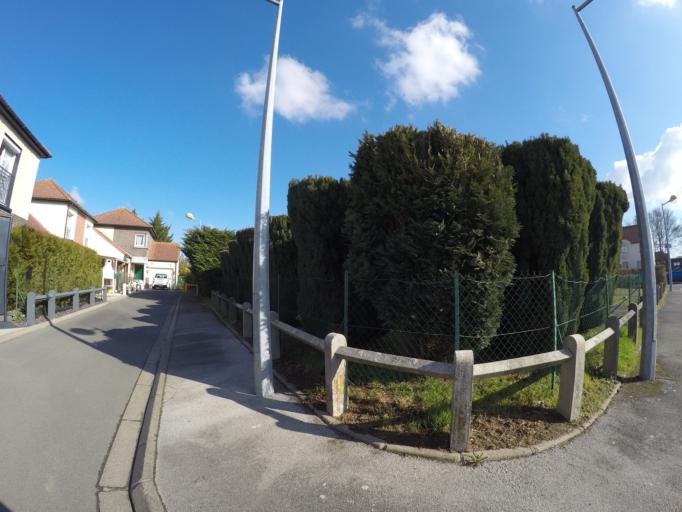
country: FR
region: Nord-Pas-de-Calais
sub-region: Departement du Pas-de-Calais
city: Mazingarbe
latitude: 50.4588
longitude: 2.7218
